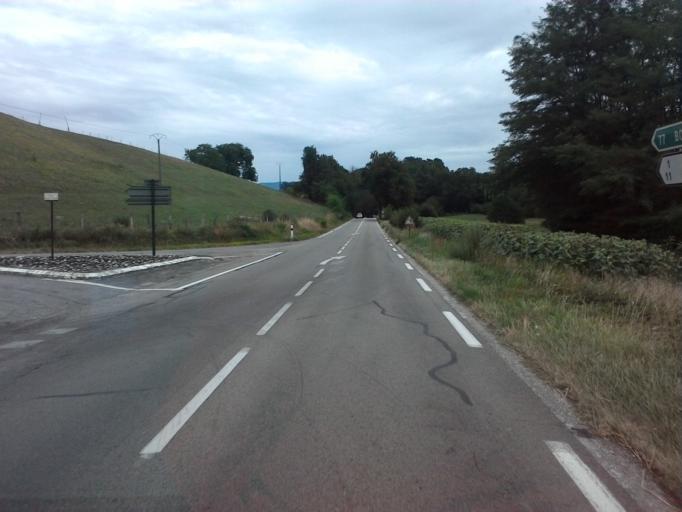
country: FR
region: Rhone-Alpes
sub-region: Departement de l'Isere
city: Corbelin
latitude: 45.6019
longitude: 5.5352
